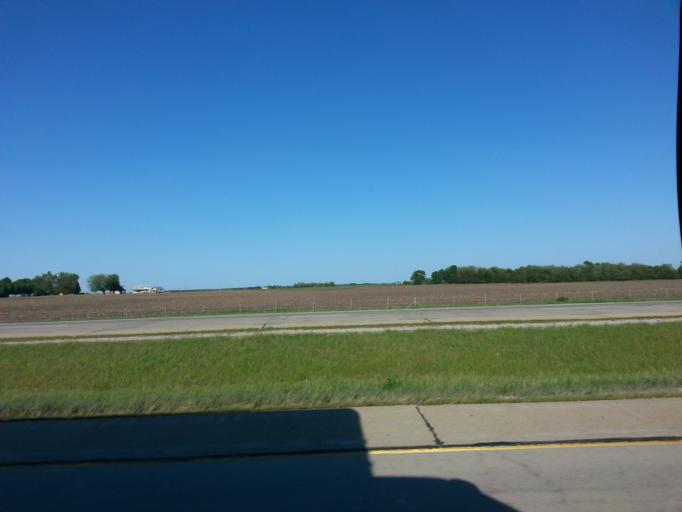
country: US
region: Illinois
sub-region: McLean County
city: Hudson
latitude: 40.6326
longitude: -89.0039
